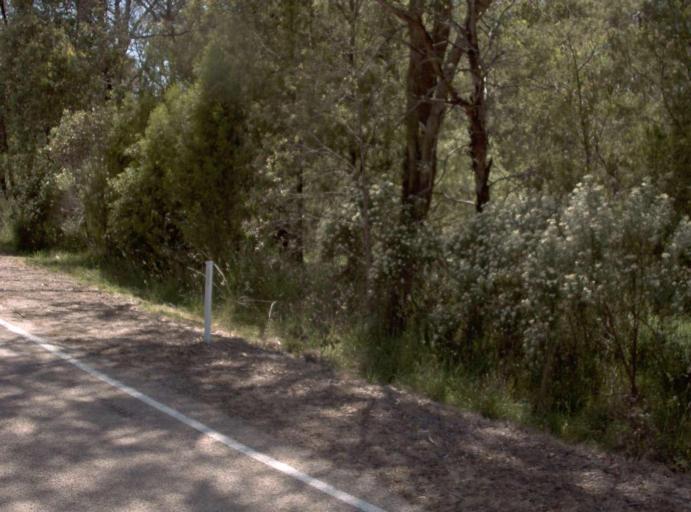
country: AU
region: Victoria
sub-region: East Gippsland
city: Lakes Entrance
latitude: -37.3339
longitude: 148.2326
